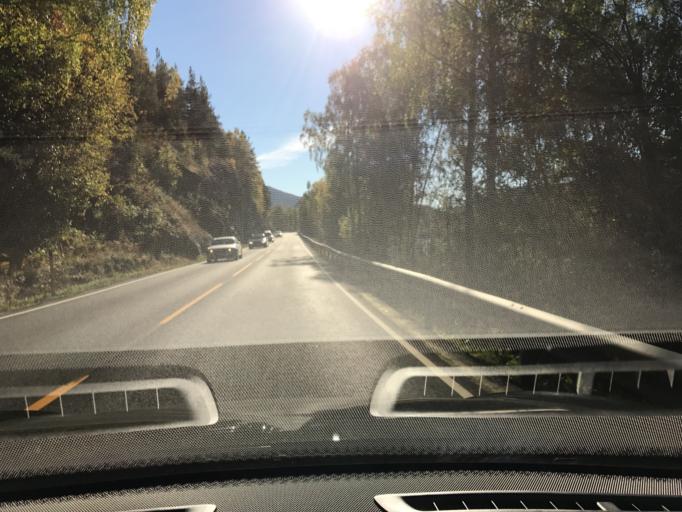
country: NO
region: Buskerud
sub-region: Krodsherad
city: Noresund
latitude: 60.3041
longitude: 9.6784
